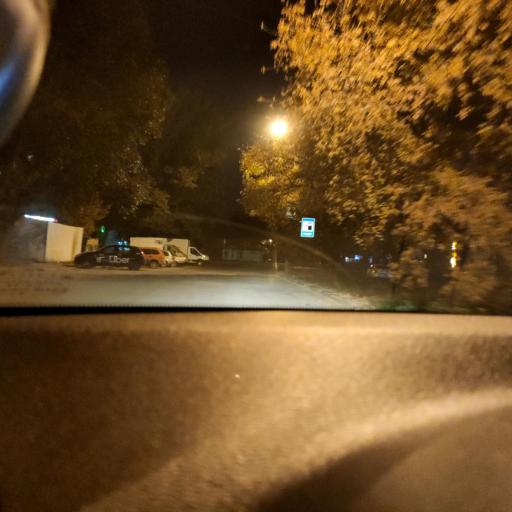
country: RU
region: Samara
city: Smyshlyayevka
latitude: 53.2281
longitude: 50.2982
